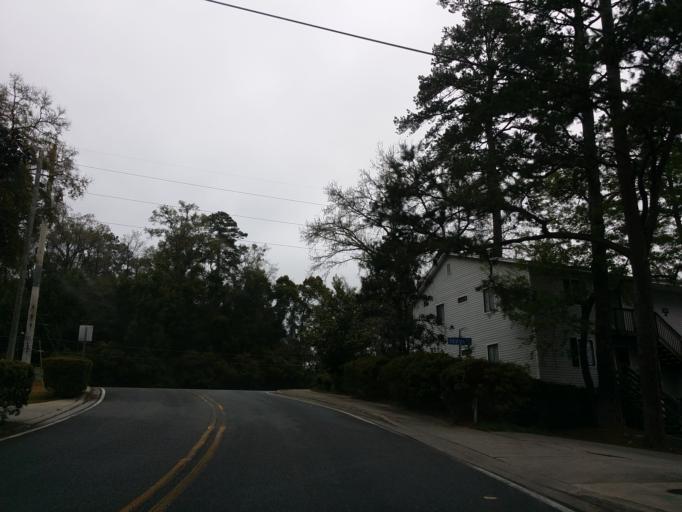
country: US
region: Florida
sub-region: Leon County
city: Tallahassee
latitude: 30.4561
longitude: -84.2553
